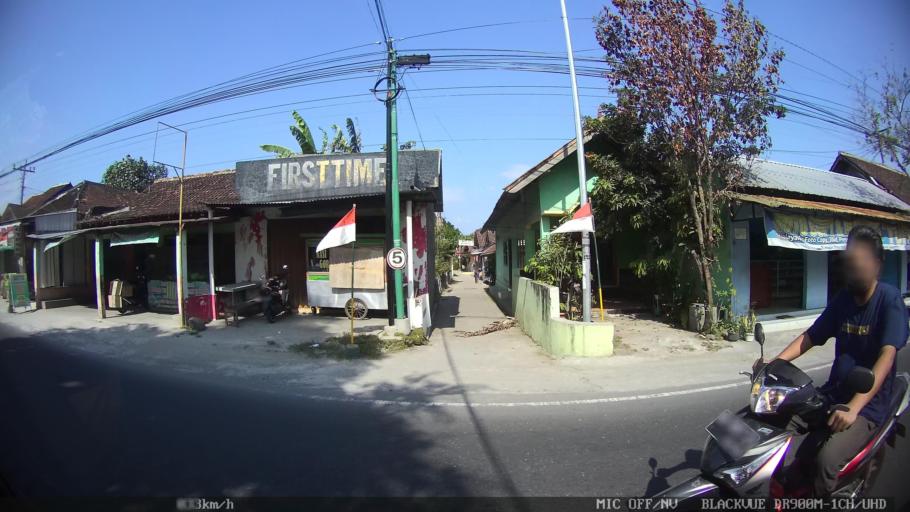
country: ID
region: Daerah Istimewa Yogyakarta
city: Sewon
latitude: -7.8775
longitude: 110.3910
